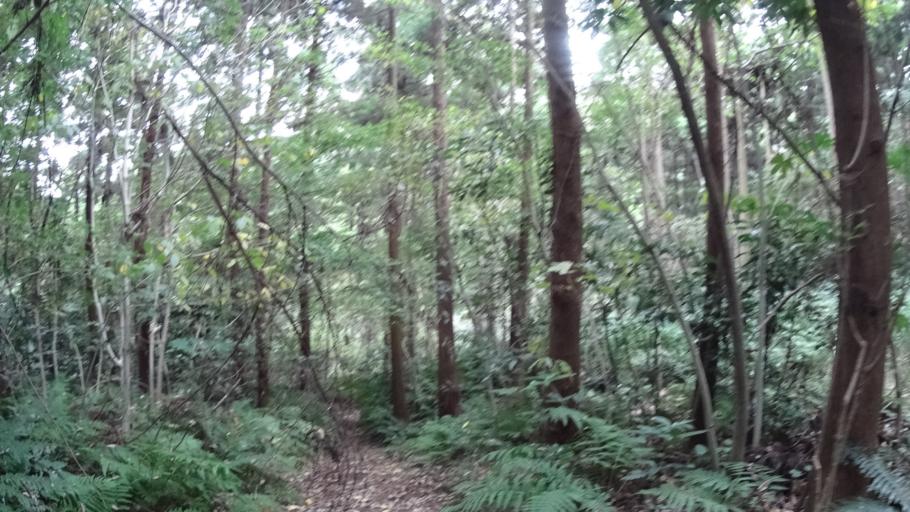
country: JP
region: Kanagawa
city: Zushi
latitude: 35.2932
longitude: 139.6208
